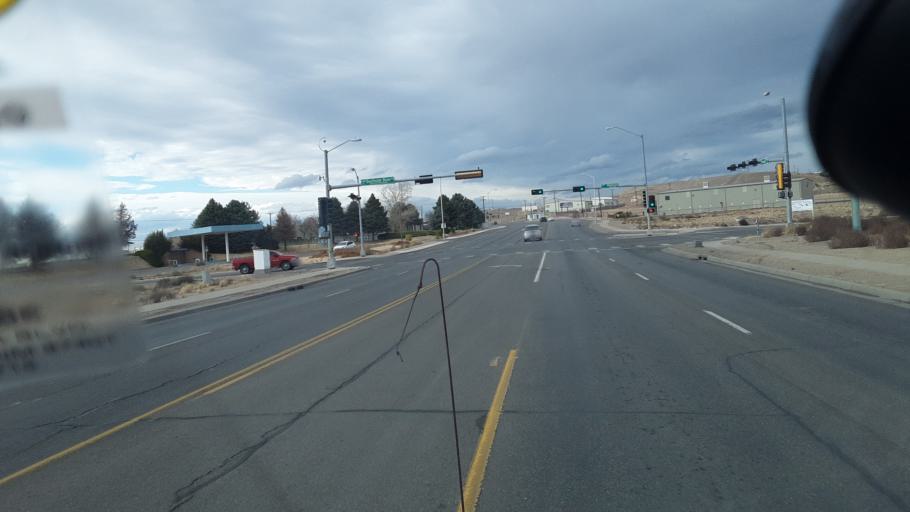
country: US
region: New Mexico
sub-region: San Juan County
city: Farmington
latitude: 36.7265
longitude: -108.1602
